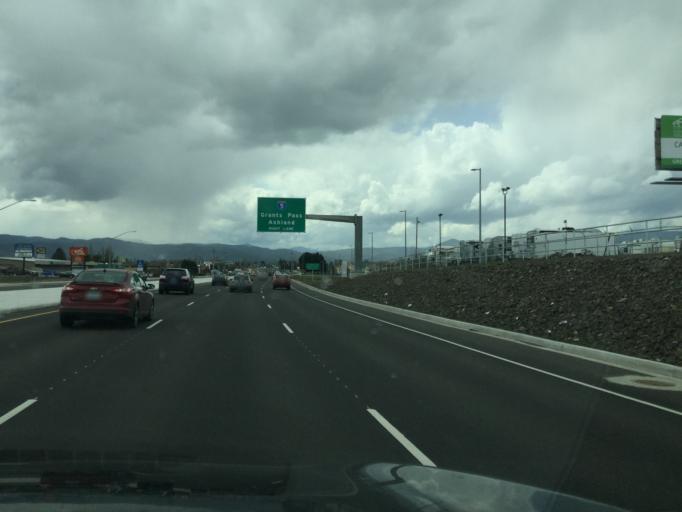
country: US
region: Oregon
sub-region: Jackson County
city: Medford
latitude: 42.3568
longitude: -122.8662
